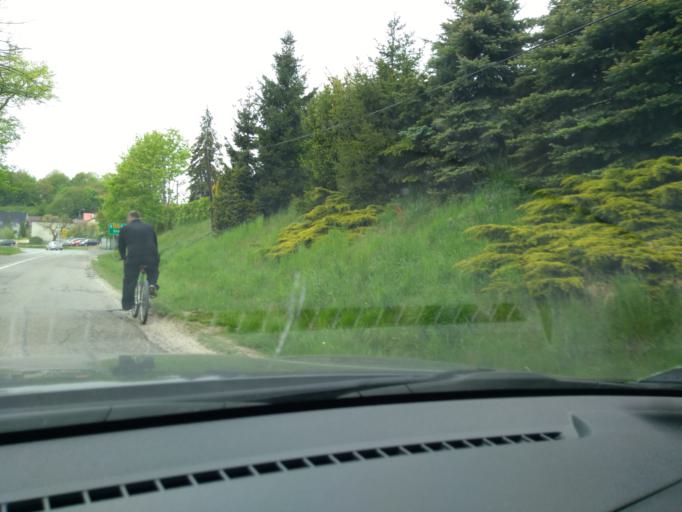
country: PL
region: Pomeranian Voivodeship
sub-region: Powiat kartuski
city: Kartuzy
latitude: 54.3528
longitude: 18.2201
